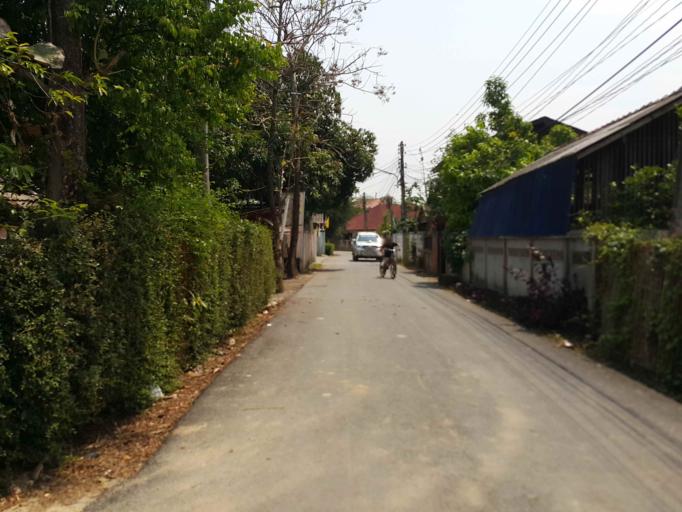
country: TH
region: Chiang Mai
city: San Kamphaeng
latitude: 18.7896
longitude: 99.0982
